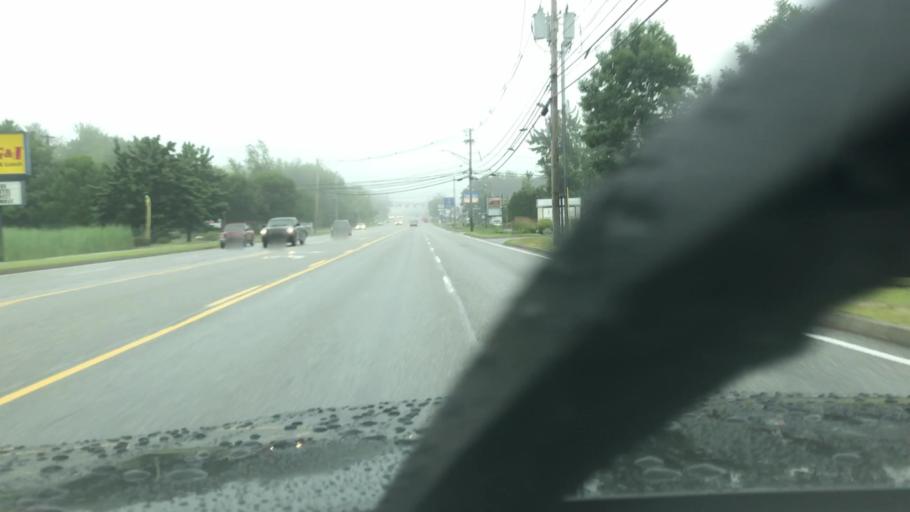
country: US
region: Maine
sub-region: Cumberland County
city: Scarborough
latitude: 43.5944
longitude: -70.3274
